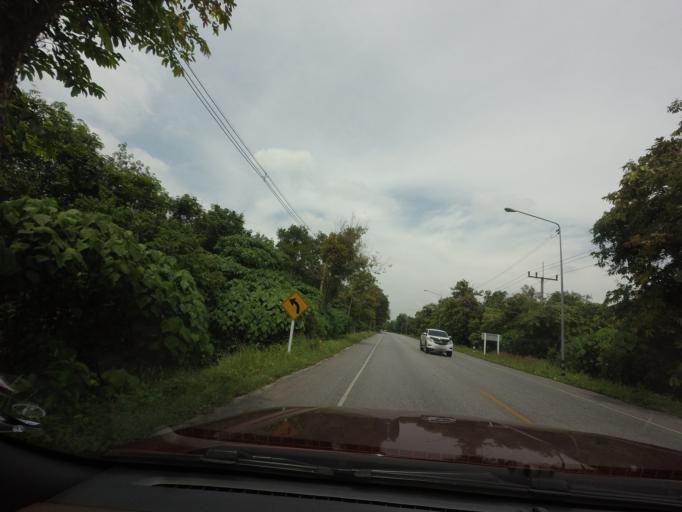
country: TH
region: Pattani
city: Mae Lan
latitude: 6.6355
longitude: 101.3021
